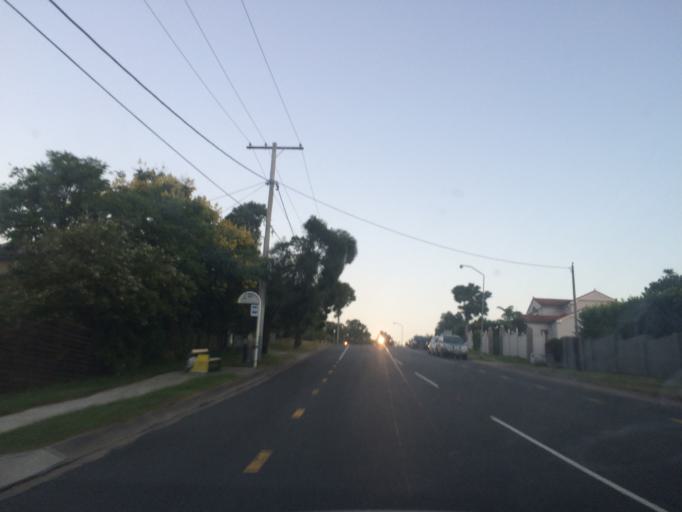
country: AU
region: Queensland
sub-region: Brisbane
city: Kenmore Hills
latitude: -27.5070
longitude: 152.9421
